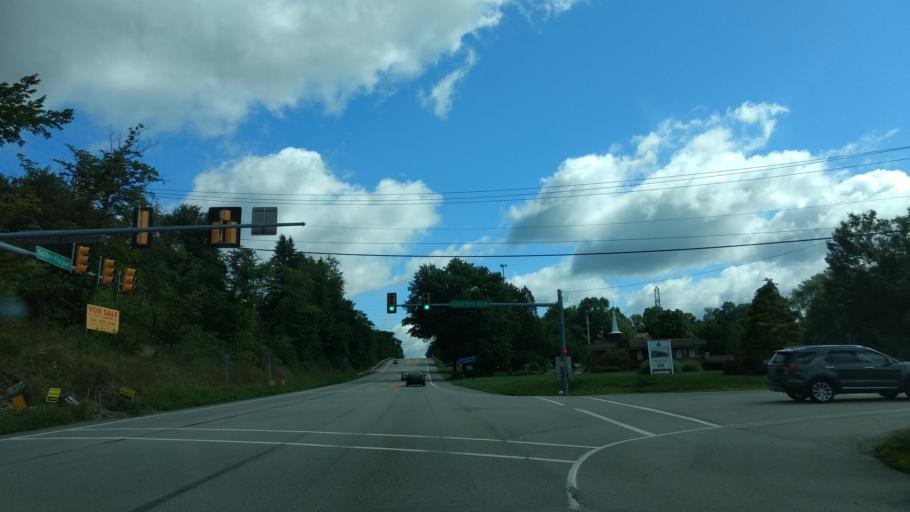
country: US
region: Pennsylvania
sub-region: Allegheny County
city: Plum
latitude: 40.4873
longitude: -79.6971
